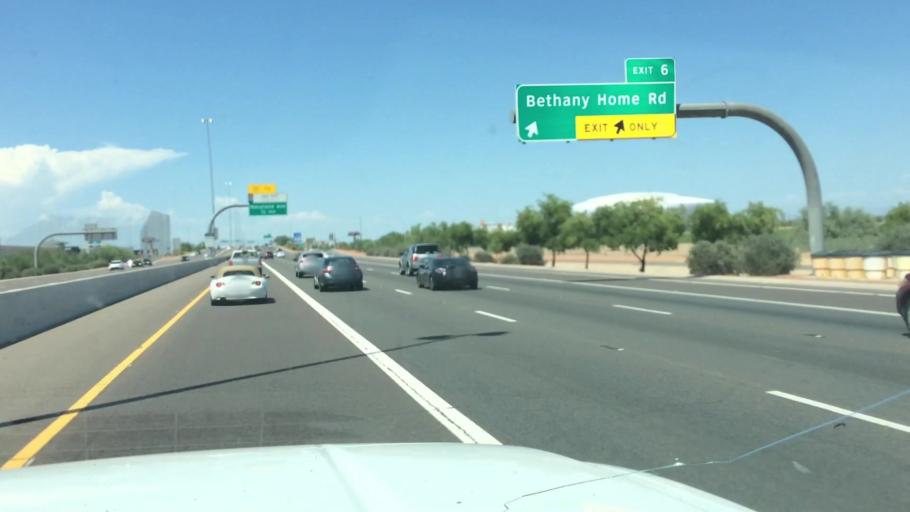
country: US
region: Arizona
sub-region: Maricopa County
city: Tolleson
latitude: 33.5167
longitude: -112.2672
